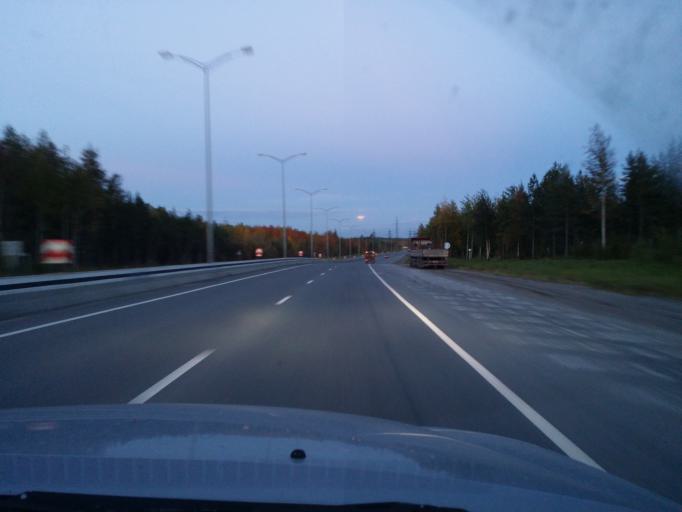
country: RU
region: Khanty-Mansiyskiy Avtonomnyy Okrug
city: Nizhnevartovsk
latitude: 60.9872
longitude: 76.4644
